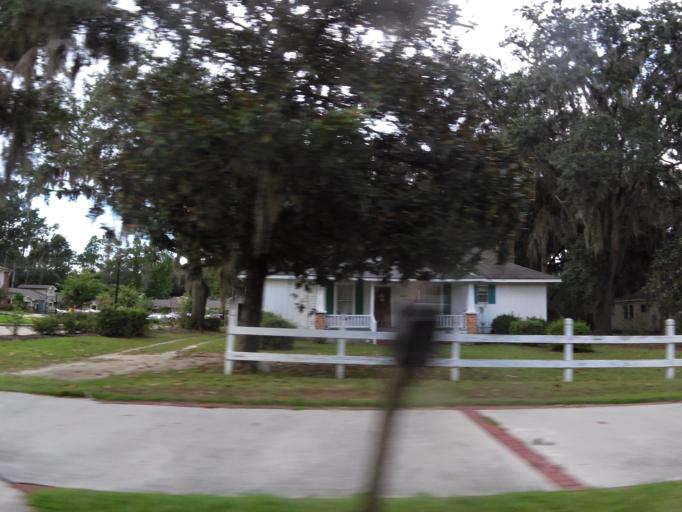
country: US
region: Georgia
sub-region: Liberty County
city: Hinesville
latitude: 31.8497
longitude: -81.5936
